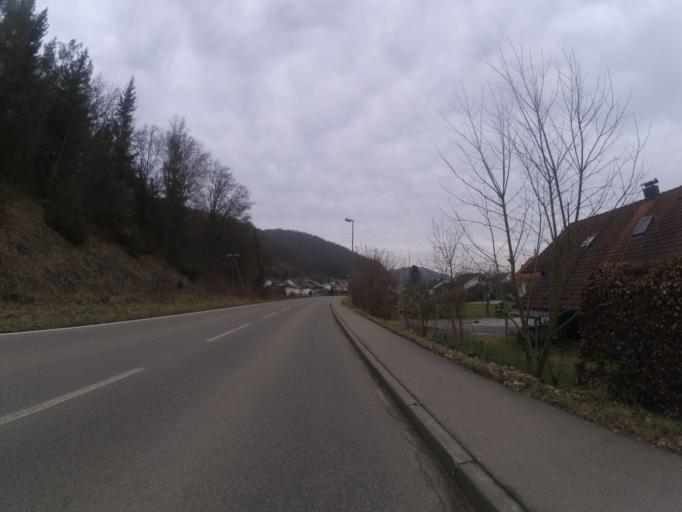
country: DE
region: Baden-Wuerttemberg
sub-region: Tuebingen Region
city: Schelklingen
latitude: 48.3663
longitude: 9.7088
